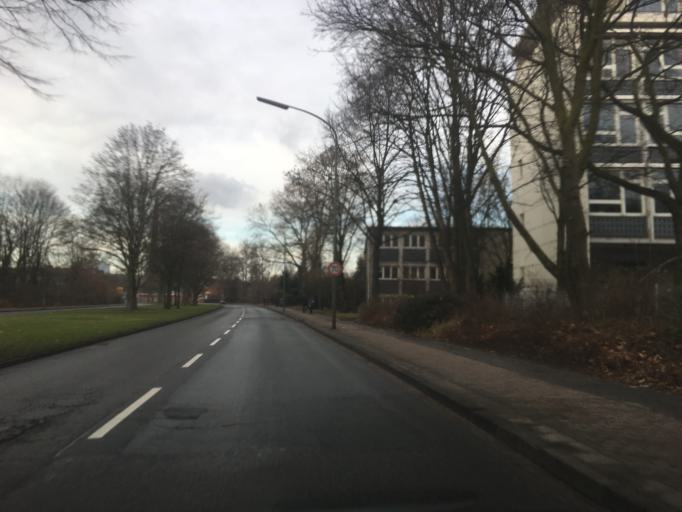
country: DE
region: North Rhine-Westphalia
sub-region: Regierungsbezirk Munster
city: Gelsenkirchen
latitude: 51.5165
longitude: 7.0869
